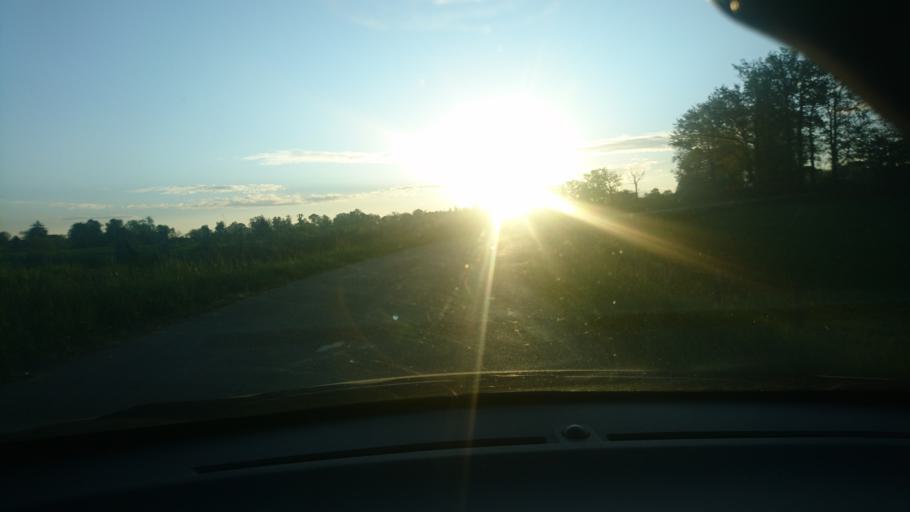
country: FR
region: Limousin
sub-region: Departement de la Haute-Vienne
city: Boisseuil
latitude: 45.7414
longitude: 1.3198
